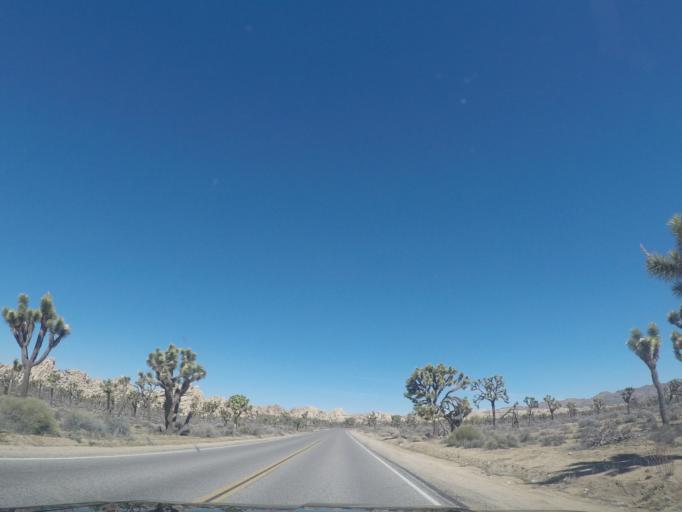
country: US
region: California
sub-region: San Bernardino County
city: Twentynine Palms
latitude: 34.0038
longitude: -116.1639
